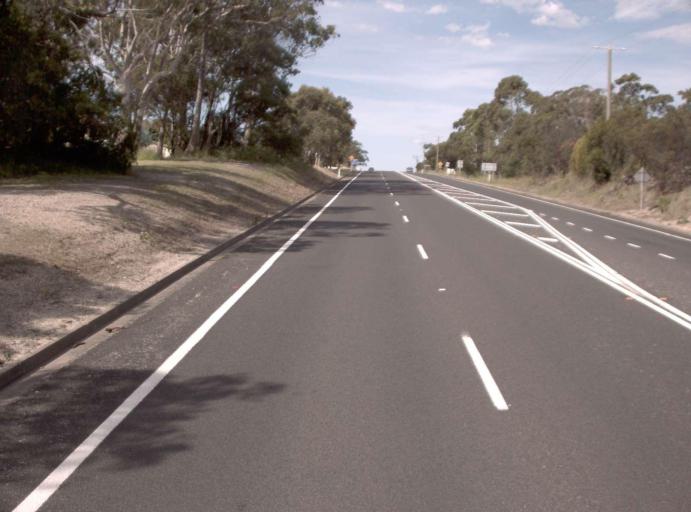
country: AU
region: Victoria
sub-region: East Gippsland
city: Lakes Entrance
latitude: -37.8646
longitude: 148.0222
